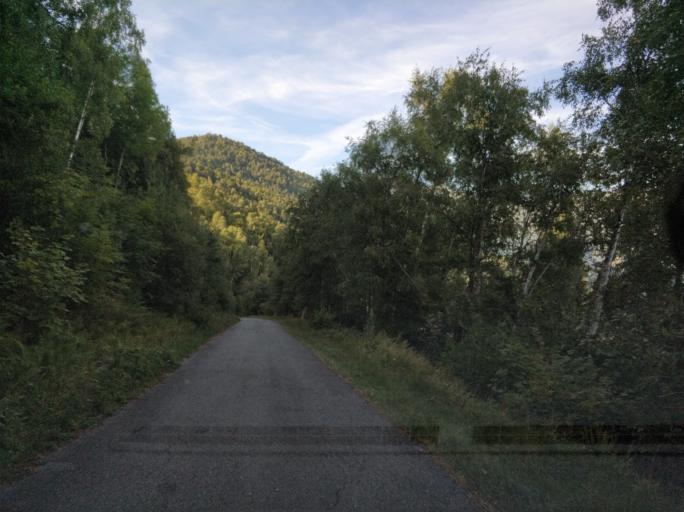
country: IT
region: Piedmont
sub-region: Provincia di Torino
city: Monastero di Lanzo
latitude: 45.3084
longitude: 7.4220
